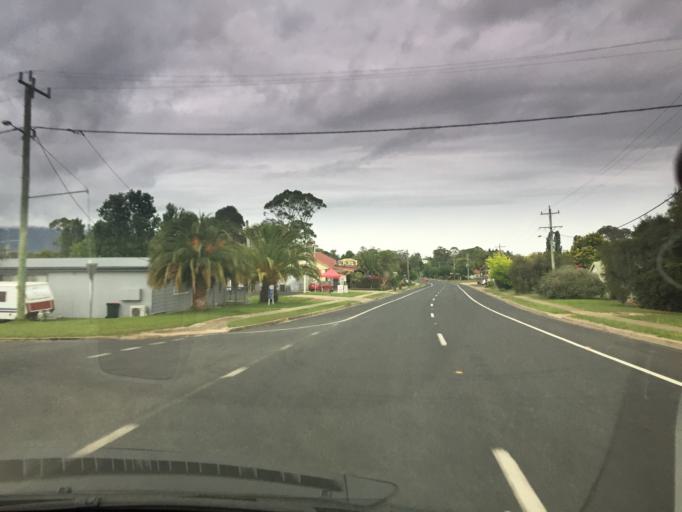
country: AU
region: New South Wales
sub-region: Bega Valley
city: Bega
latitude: -36.6265
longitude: 149.5675
